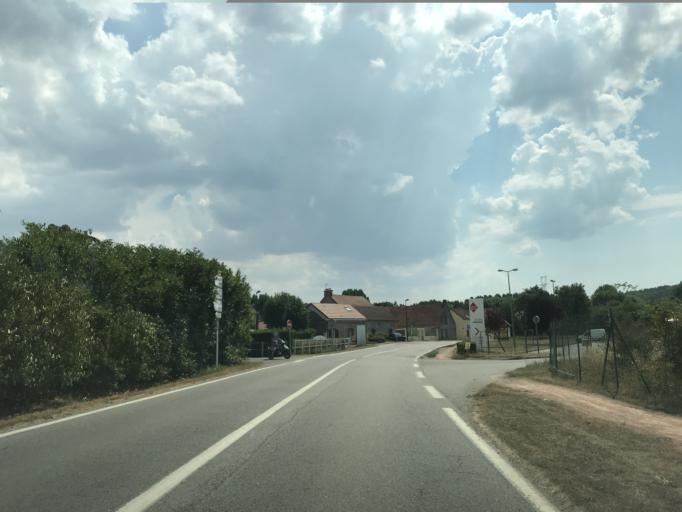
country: FR
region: Haute-Normandie
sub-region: Departement de l'Eure
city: Garennes-sur-Eure
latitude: 48.9138
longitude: 1.4449
